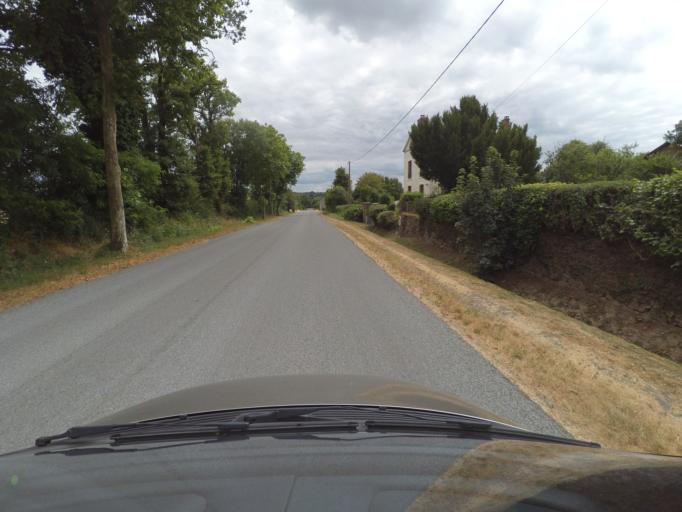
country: FR
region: Limousin
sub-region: Departement de la Haute-Vienne
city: Arnac-la-Poste
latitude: 46.2397
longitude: 1.3817
